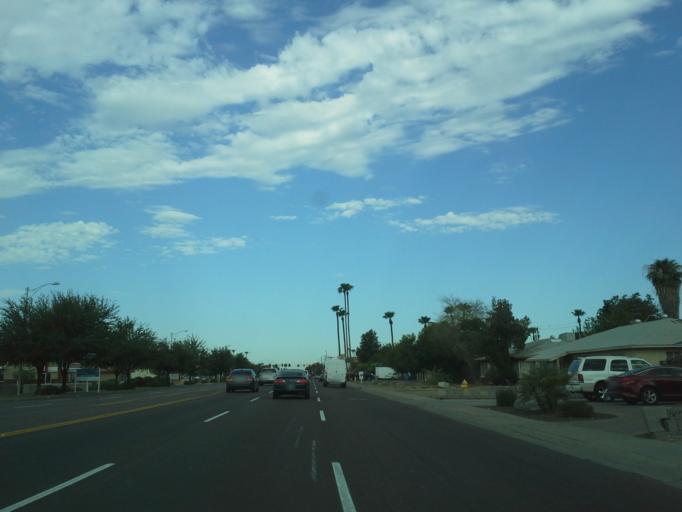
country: US
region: Arizona
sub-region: Maricopa County
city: Phoenix
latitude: 33.5241
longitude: -112.0959
